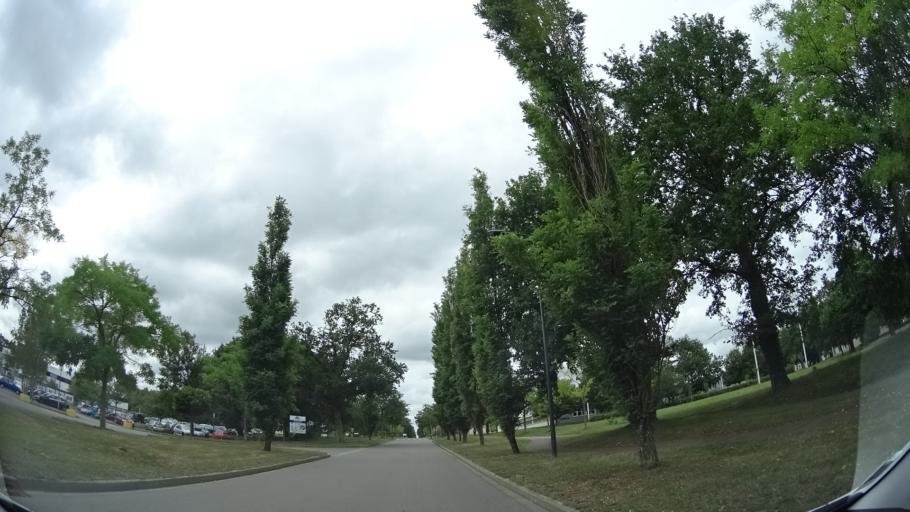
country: FR
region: Brittany
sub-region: Departement d'Ille-et-Vilaine
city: Bruz
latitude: 48.0455
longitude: -1.7436
